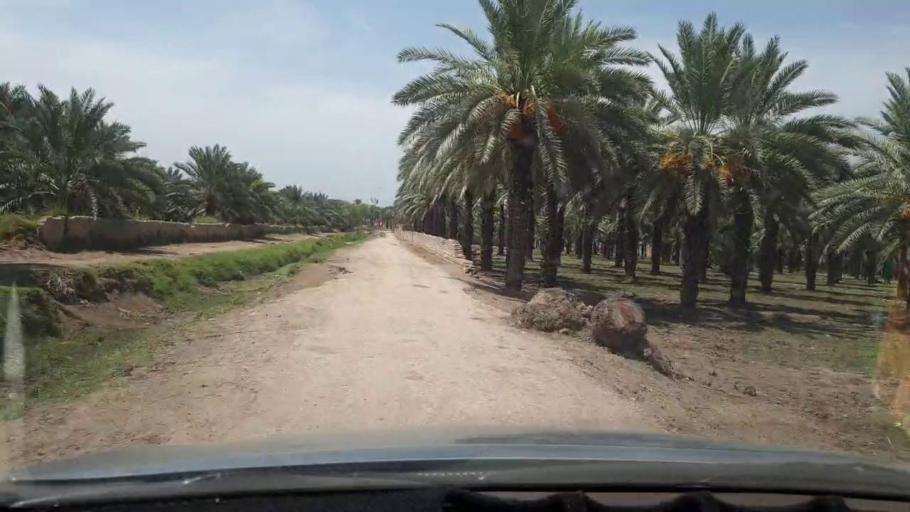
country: PK
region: Sindh
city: Khairpur
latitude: 27.4799
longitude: 68.7686
